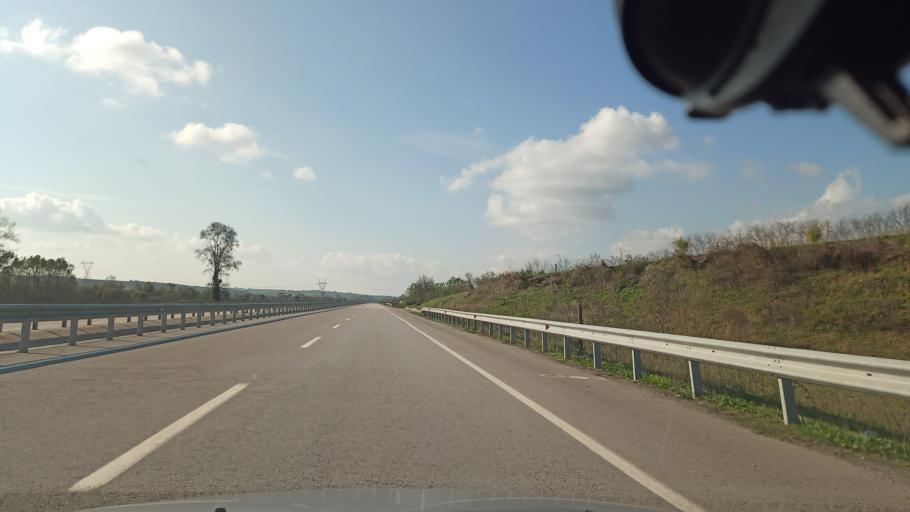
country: TR
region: Sakarya
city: Kaynarca
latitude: 41.0833
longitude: 30.4170
